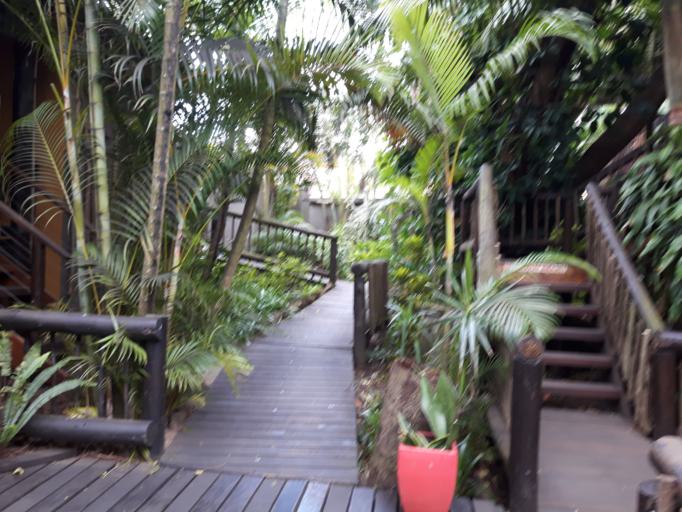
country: ZA
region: KwaZulu-Natal
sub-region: uMkhanyakude District Municipality
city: Mtubatuba
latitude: -28.3781
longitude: 32.4122
